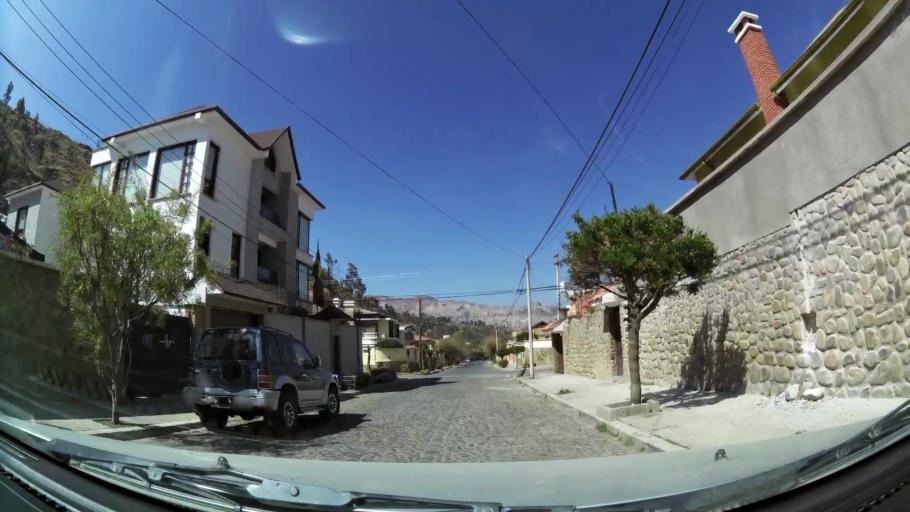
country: BO
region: La Paz
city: La Paz
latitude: -16.5250
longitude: -68.0848
